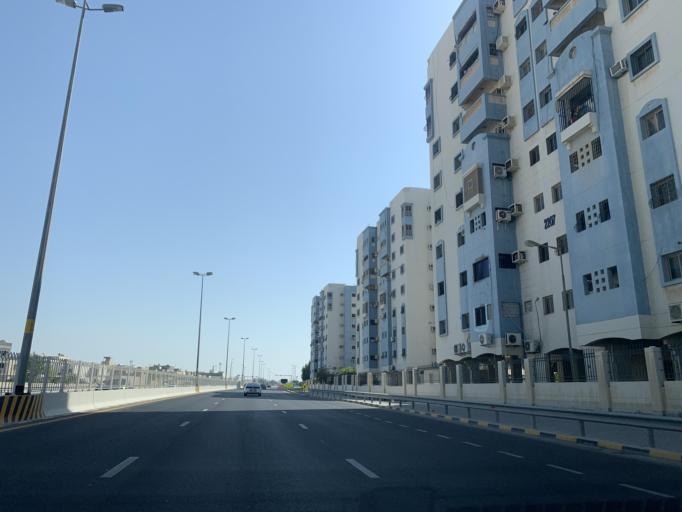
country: BH
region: Central Governorate
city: Madinat Hamad
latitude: 26.1163
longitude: 50.4902
